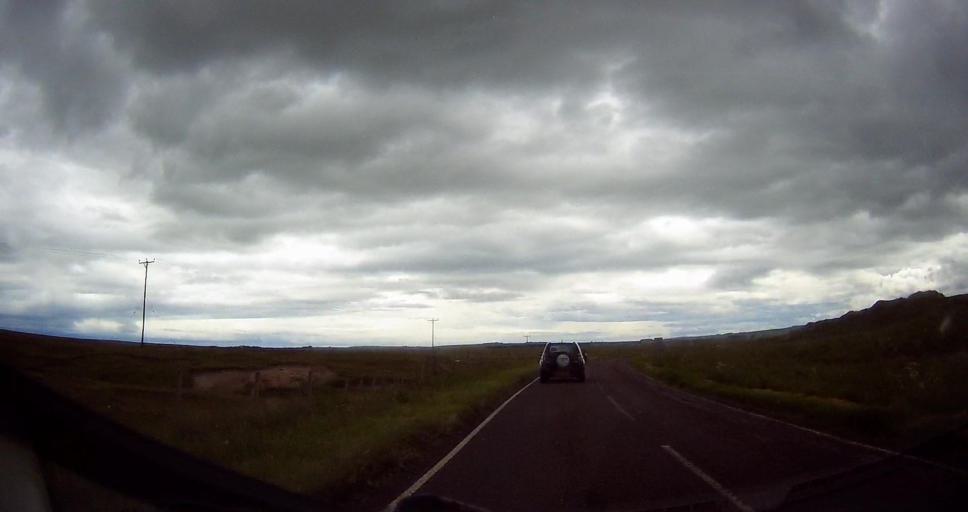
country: GB
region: Scotland
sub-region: Highland
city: Thurso
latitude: 58.6088
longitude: -3.3437
